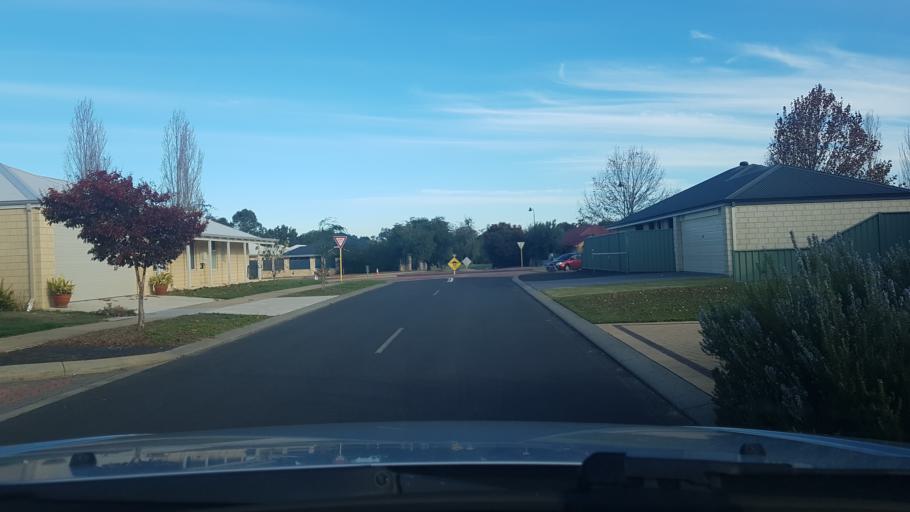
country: AU
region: Western Australia
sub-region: Busselton
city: Vasse
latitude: -33.6776
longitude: 115.2581
